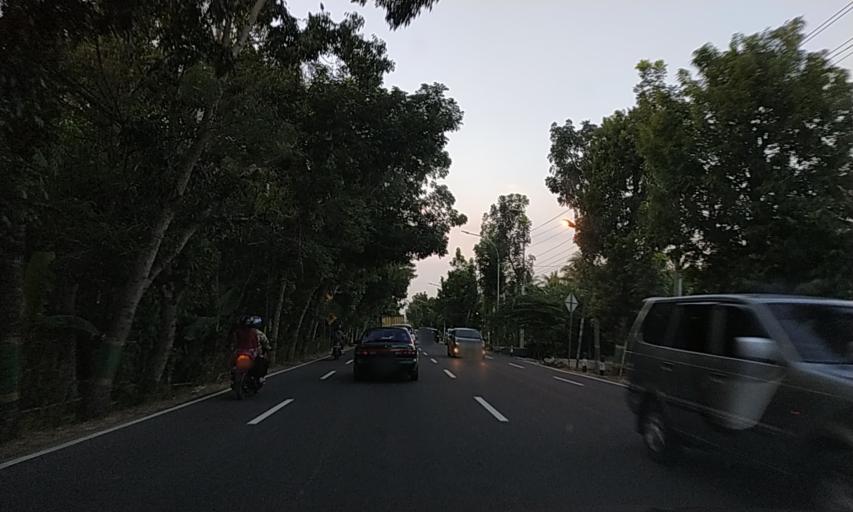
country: ID
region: Daerah Istimewa Yogyakarta
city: Srandakan
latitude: -7.8861
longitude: 110.1307
